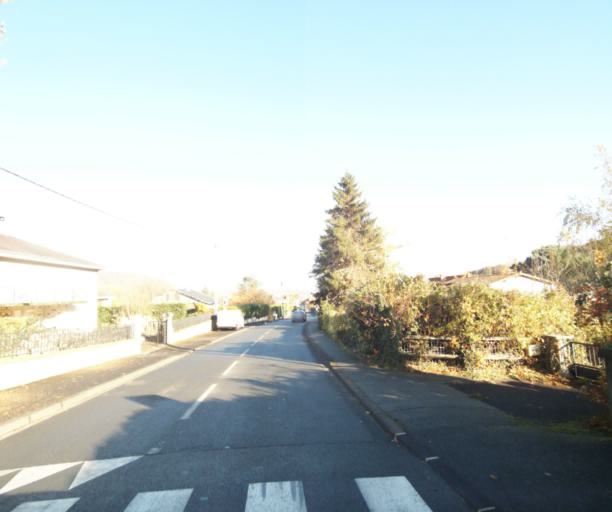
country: FR
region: Auvergne
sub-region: Departement du Puy-de-Dome
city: Nohanent
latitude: 45.8028
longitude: 3.0559
